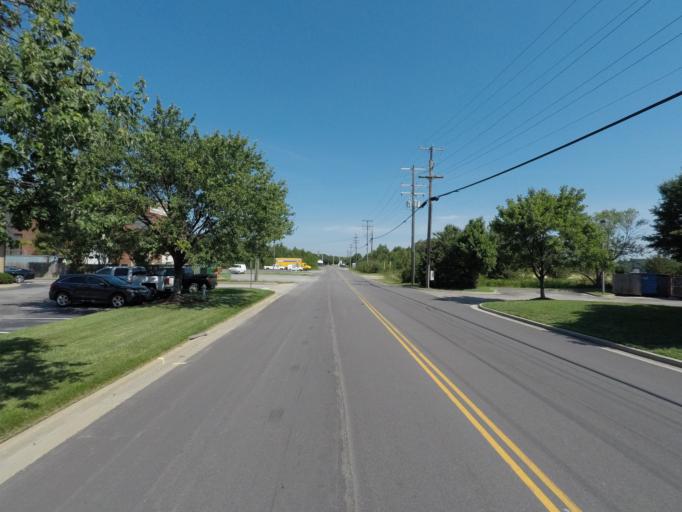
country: US
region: Virginia
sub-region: Henrico County
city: Dumbarton
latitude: 37.5838
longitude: -77.4821
